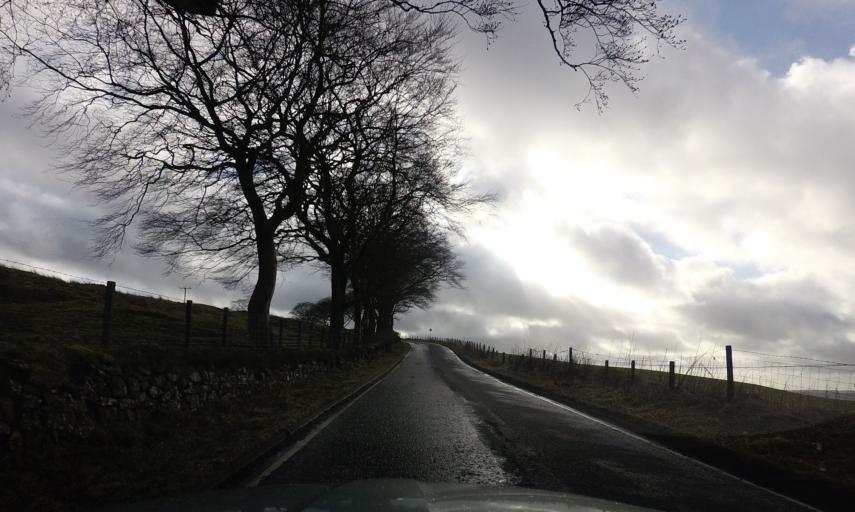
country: GB
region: Scotland
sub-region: West Lothian
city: Bathgate
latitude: 55.9290
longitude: -3.6311
